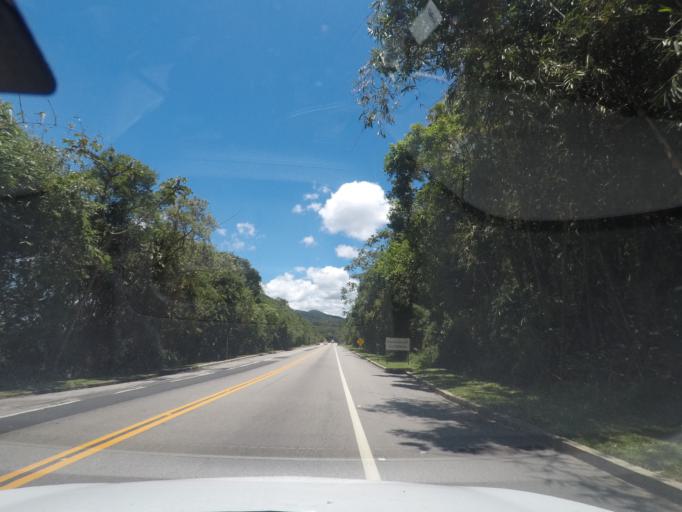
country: BR
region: Rio de Janeiro
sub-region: Teresopolis
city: Teresopolis
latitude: -22.4602
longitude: -42.9801
